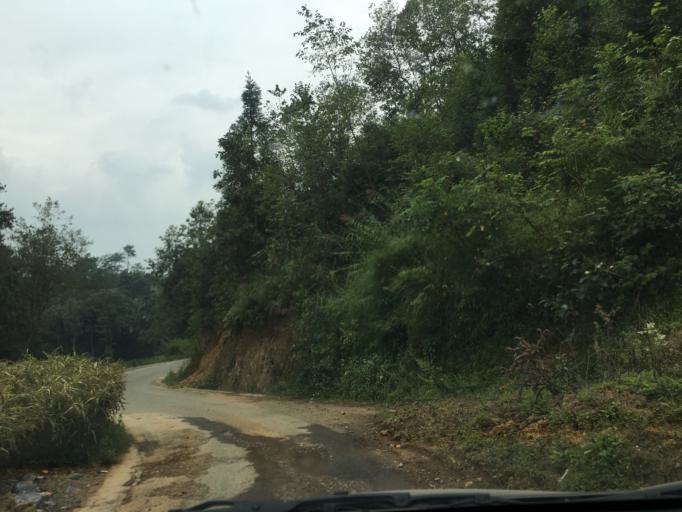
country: CN
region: Guangxi Zhuangzu Zizhiqu
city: Xinzhou
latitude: 25.5420
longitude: 105.5856
